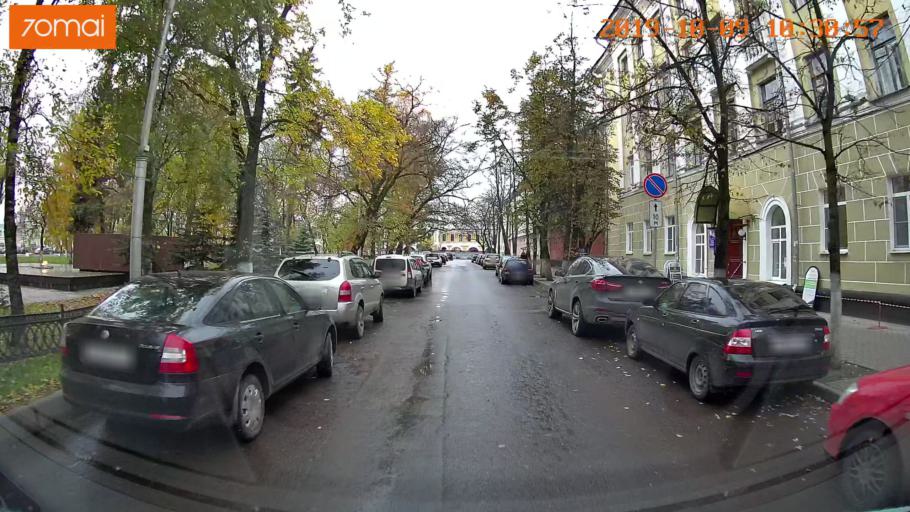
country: RU
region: Vologda
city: Vologda
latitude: 59.2200
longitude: 39.8938
